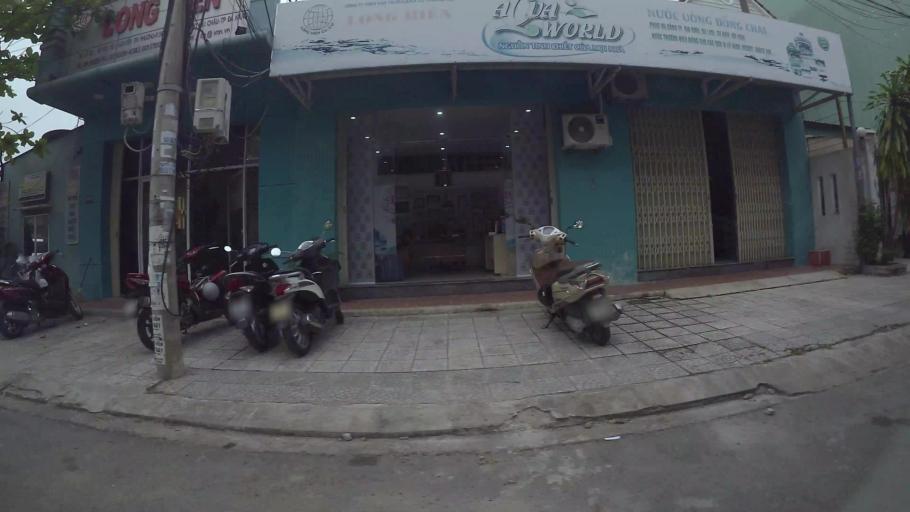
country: VN
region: Da Nang
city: Cam Le
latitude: 16.0376
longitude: 108.2080
